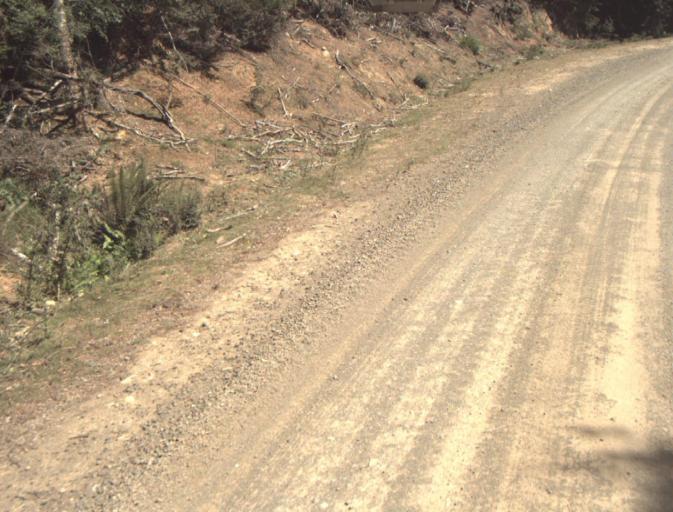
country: AU
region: Tasmania
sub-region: Dorset
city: Scottsdale
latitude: -41.3793
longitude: 147.4833
